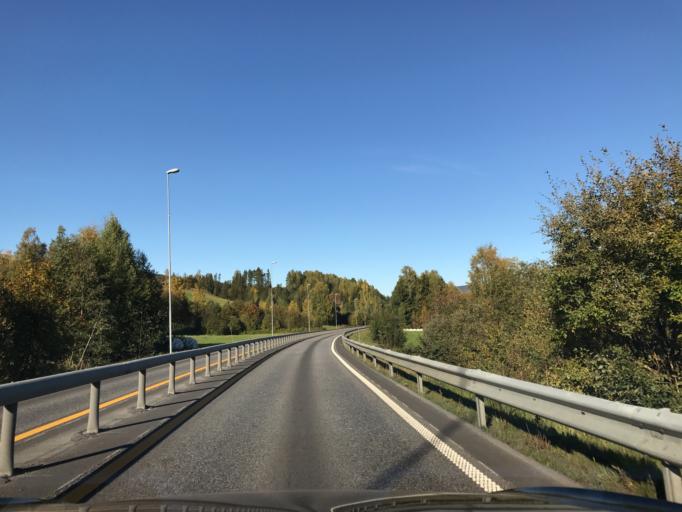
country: NO
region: Oppland
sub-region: Lillehammer
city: Lillehammer
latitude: 60.9973
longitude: 10.5051
